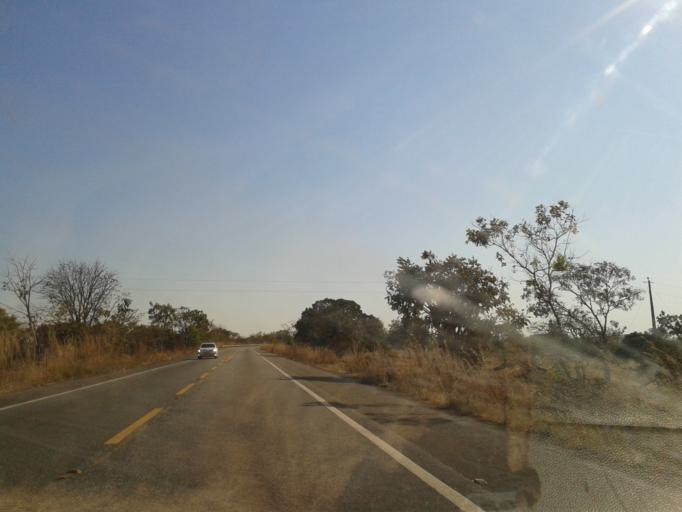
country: BR
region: Goias
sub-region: Mozarlandia
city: Mozarlandia
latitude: -14.9214
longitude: -50.5533
